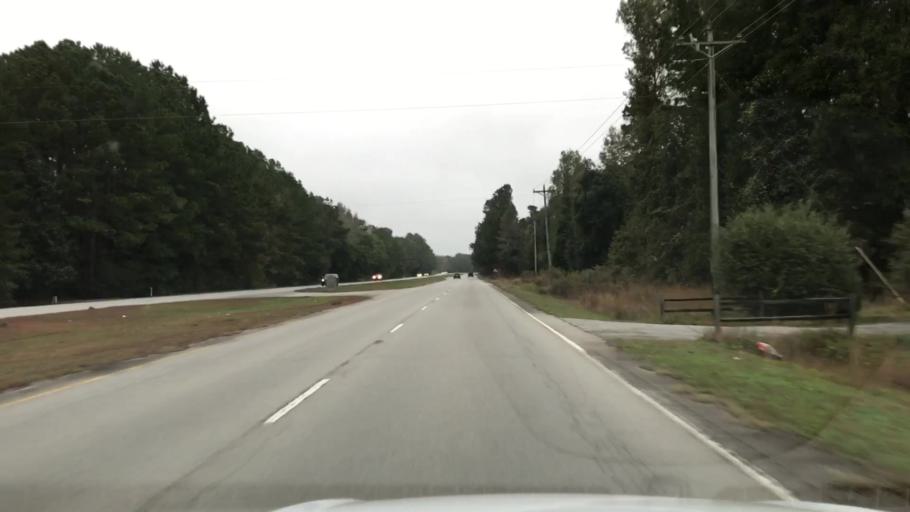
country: US
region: South Carolina
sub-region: Charleston County
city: Awendaw
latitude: 32.9948
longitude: -79.6450
